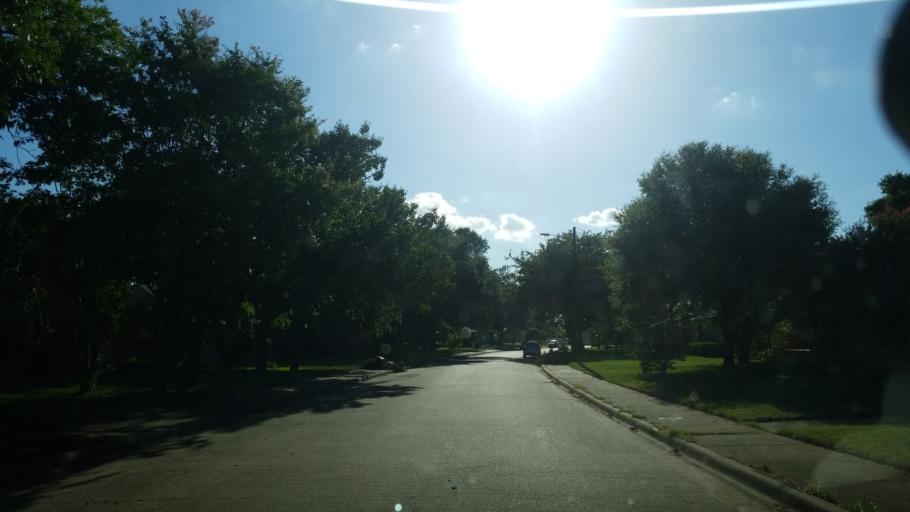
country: US
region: Texas
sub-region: Dallas County
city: Balch Springs
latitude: 32.7846
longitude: -96.7033
